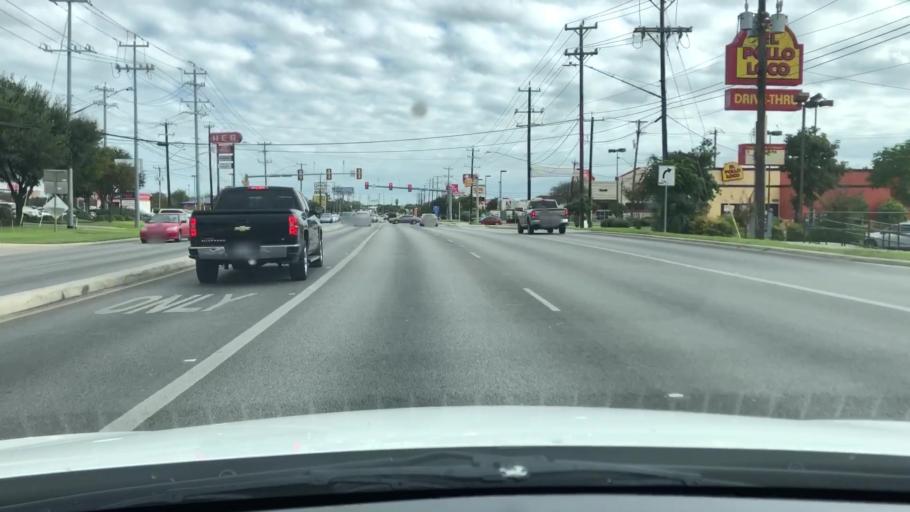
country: US
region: Texas
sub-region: Bexar County
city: Leon Valley
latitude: 29.4850
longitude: -98.6676
